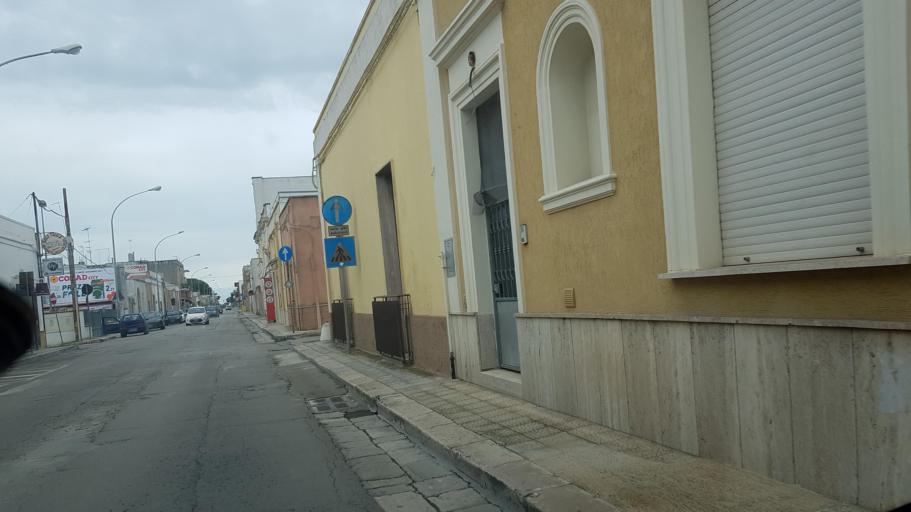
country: IT
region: Apulia
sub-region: Provincia di Lecce
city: Squinzano
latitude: 40.4357
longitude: 18.0402
